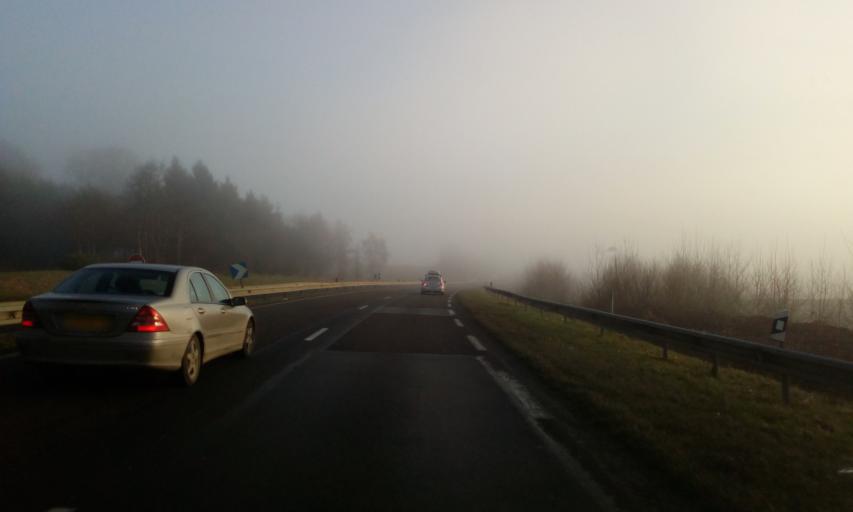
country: FR
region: Champagne-Ardenne
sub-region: Departement des Ardennes
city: Tournes
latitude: 49.7985
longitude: 4.6301
